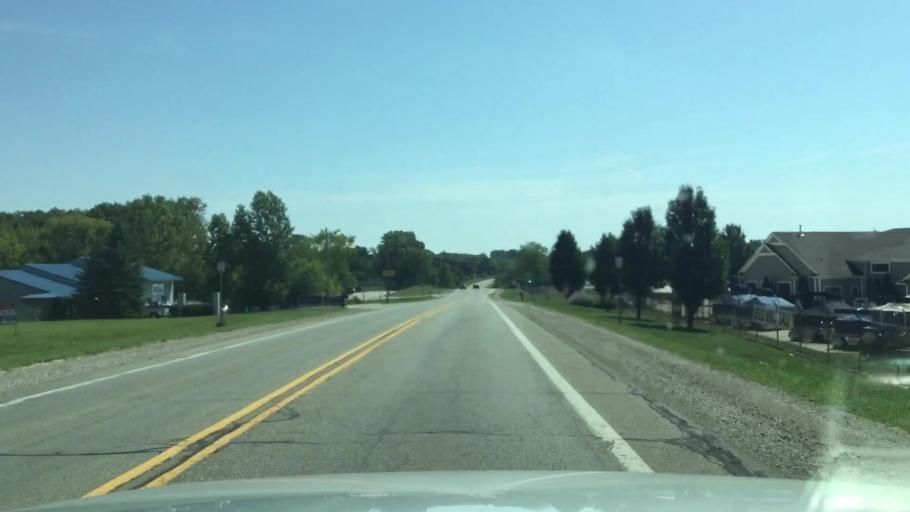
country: US
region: Michigan
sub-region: Lenawee County
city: Manitou Beach-Devils Lake
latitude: 42.0038
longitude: -84.2796
